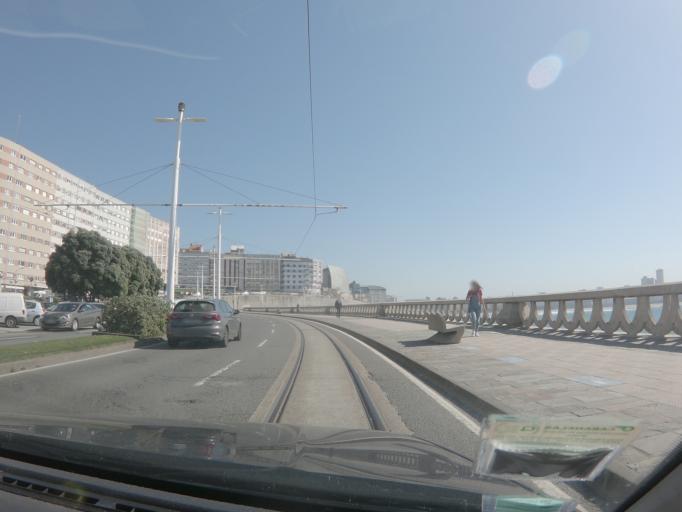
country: ES
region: Galicia
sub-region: Provincia da Coruna
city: A Coruna
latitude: 43.3800
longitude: -8.4093
